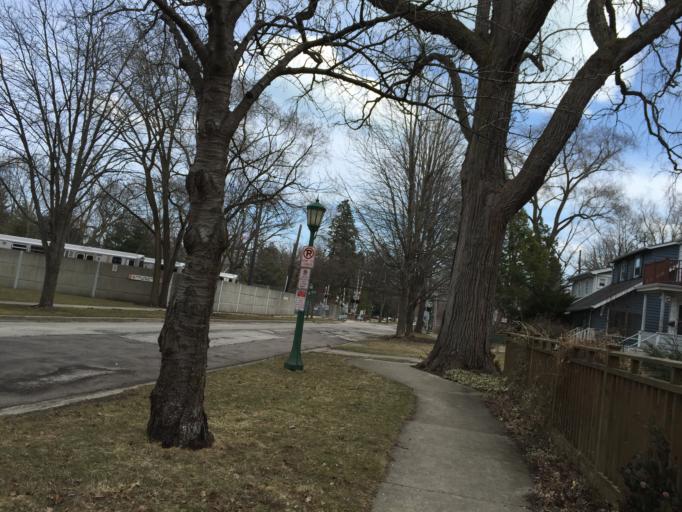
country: US
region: Illinois
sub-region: Cook County
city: Evanston
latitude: 42.0712
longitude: -87.6908
